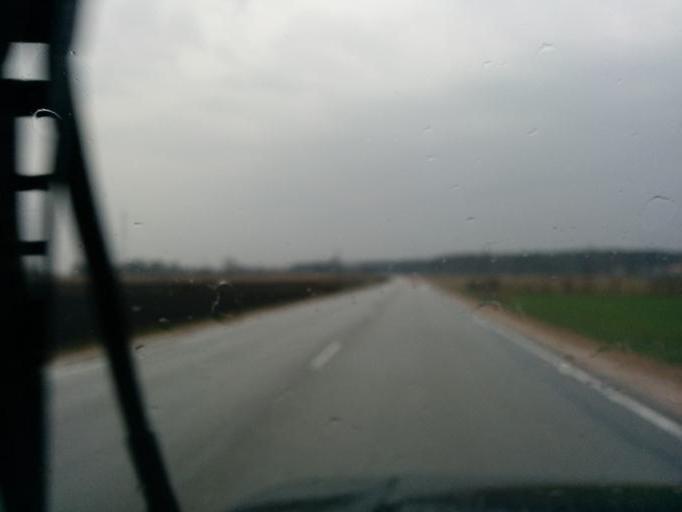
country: LV
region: Kekava
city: Kekava
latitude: 56.8107
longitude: 24.1690
